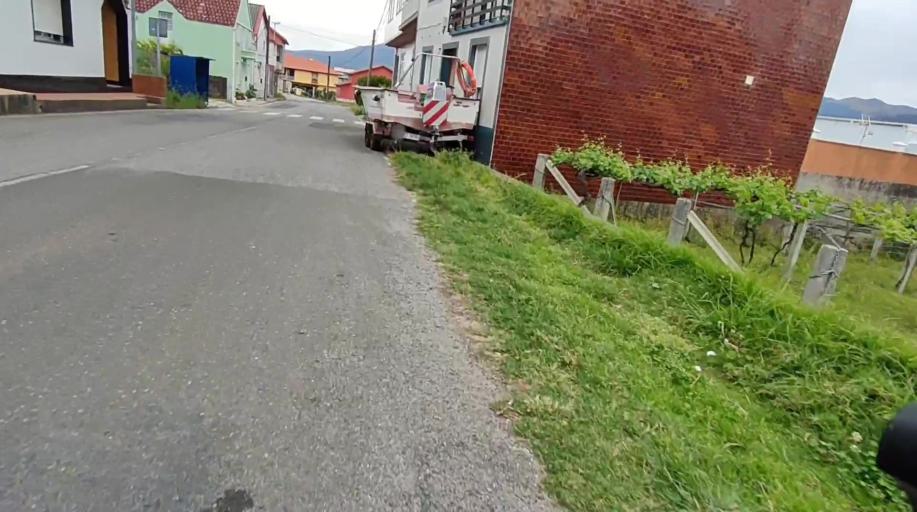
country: ES
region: Galicia
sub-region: Provincia da Coruna
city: Boiro
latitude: 42.6259
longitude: -8.8776
